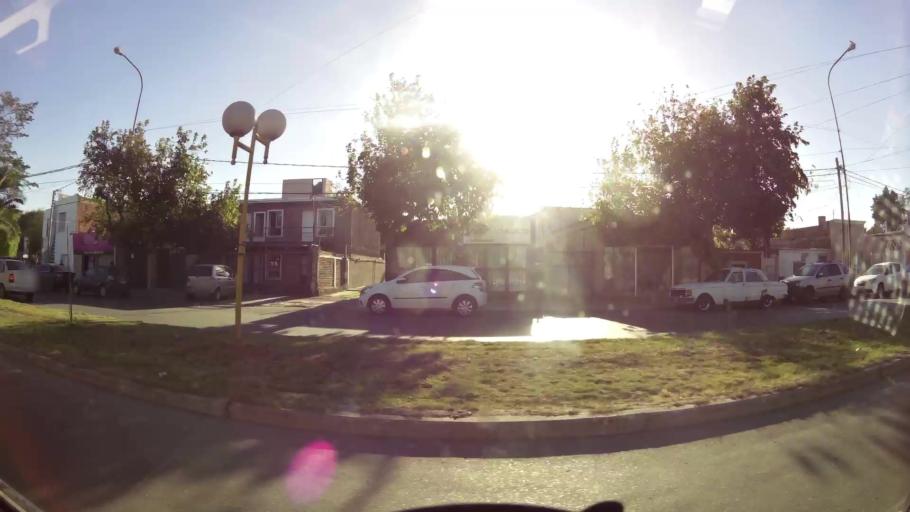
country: AR
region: San Juan
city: San Juan
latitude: -31.5503
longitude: -68.5204
